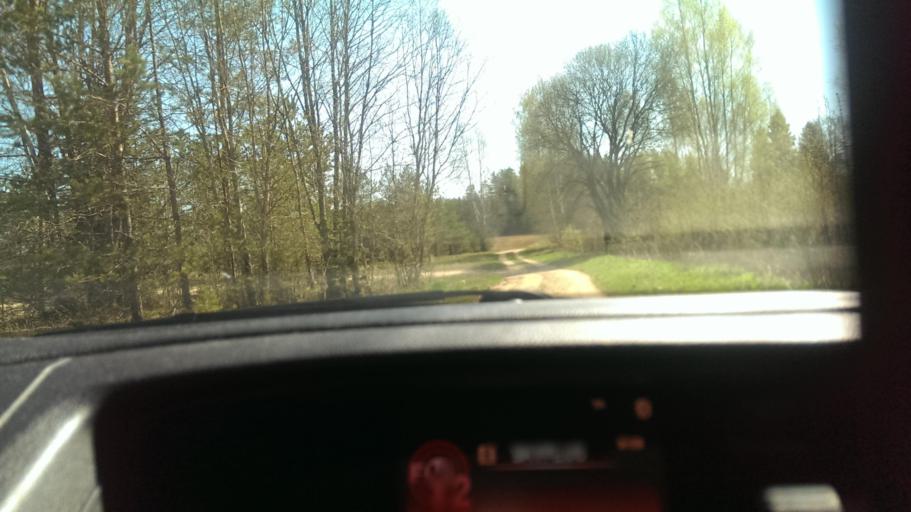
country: EE
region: Vorumaa
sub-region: Antsla vald
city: Vana-Antsla
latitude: 57.9577
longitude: 26.6952
